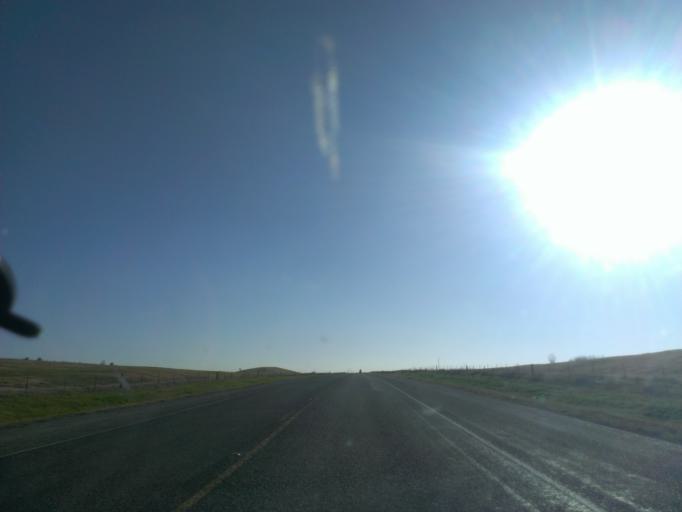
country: US
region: Texas
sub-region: Bastrop County
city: Elgin
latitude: 30.3542
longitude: -97.2719
